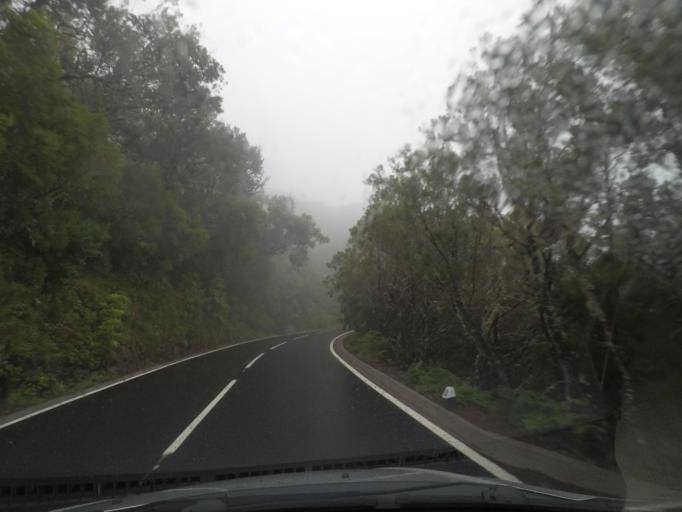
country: PT
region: Madeira
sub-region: Santana
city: Santana
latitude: 32.7676
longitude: -16.9146
